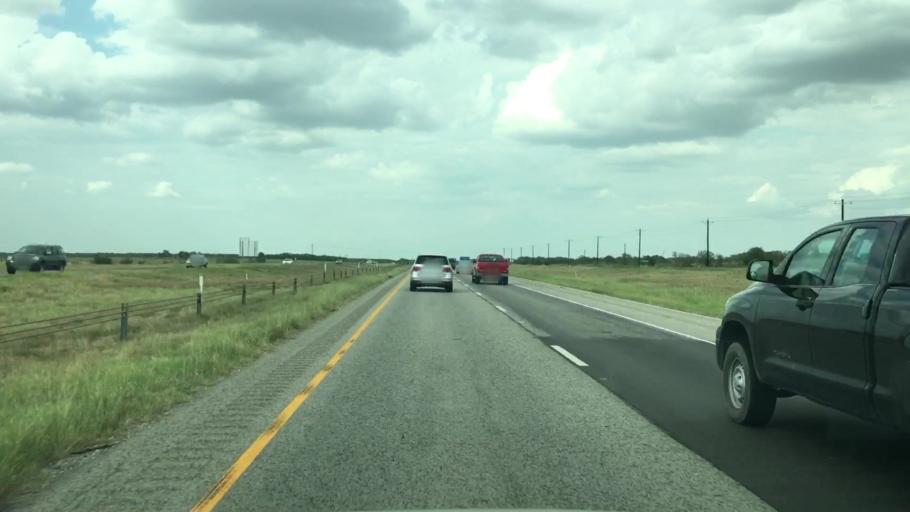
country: US
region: Texas
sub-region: Atascosa County
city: Pleasanton
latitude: 29.0114
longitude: -98.4310
